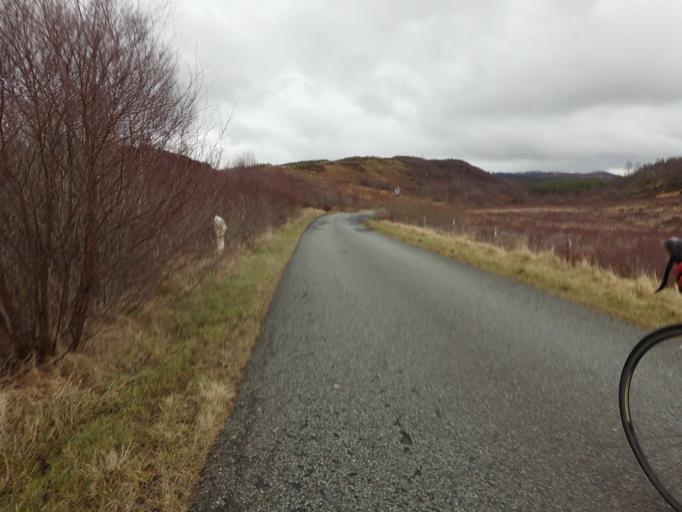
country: GB
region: Scotland
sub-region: West Dunbartonshire
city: Balloch
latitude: 56.2454
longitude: -4.5782
